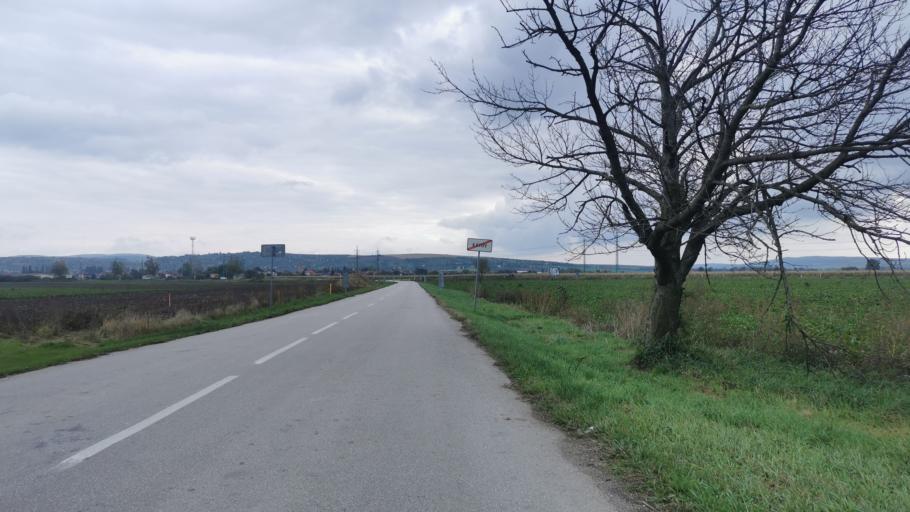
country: SK
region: Trnavsky
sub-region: Okres Skalica
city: Holic
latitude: 48.8281
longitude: 17.1775
